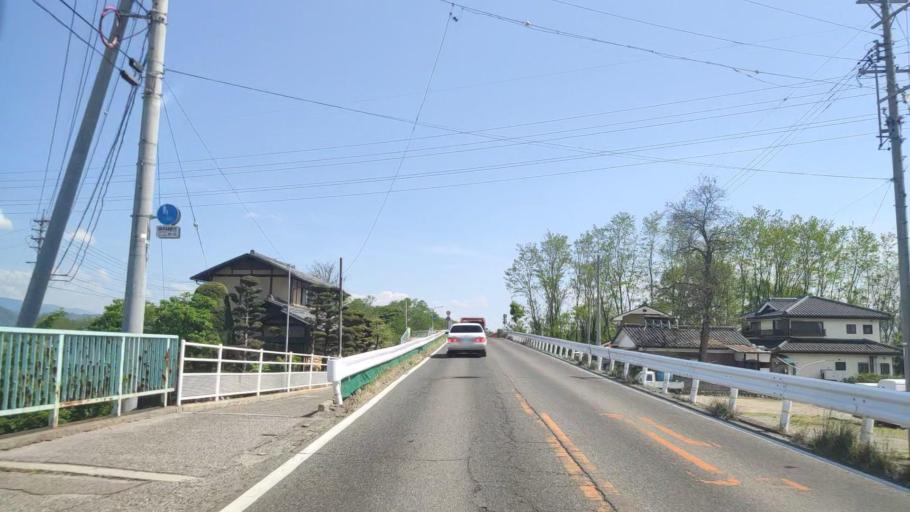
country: JP
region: Nagano
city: Hotaka
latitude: 36.3535
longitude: 137.8813
